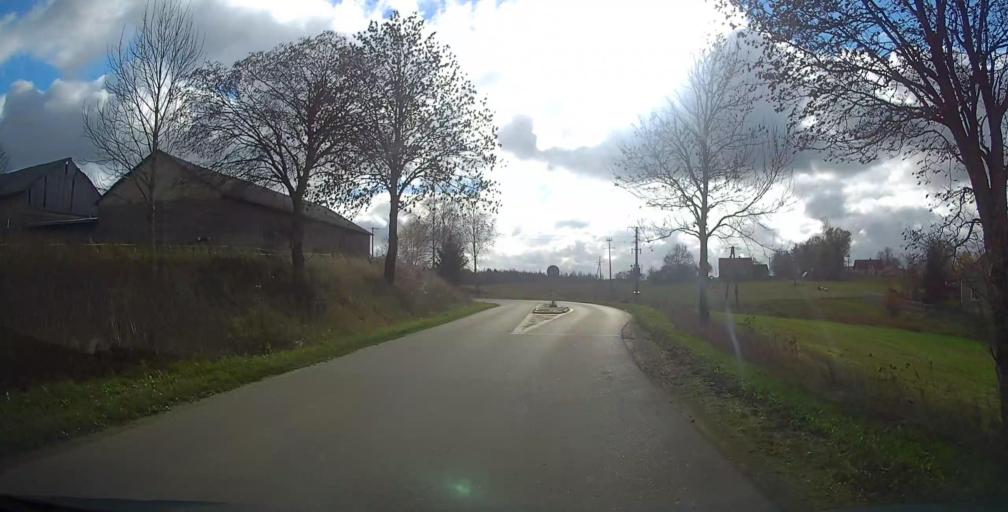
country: PL
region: Podlasie
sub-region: Suwalki
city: Suwalki
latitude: 54.3177
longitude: 22.8636
